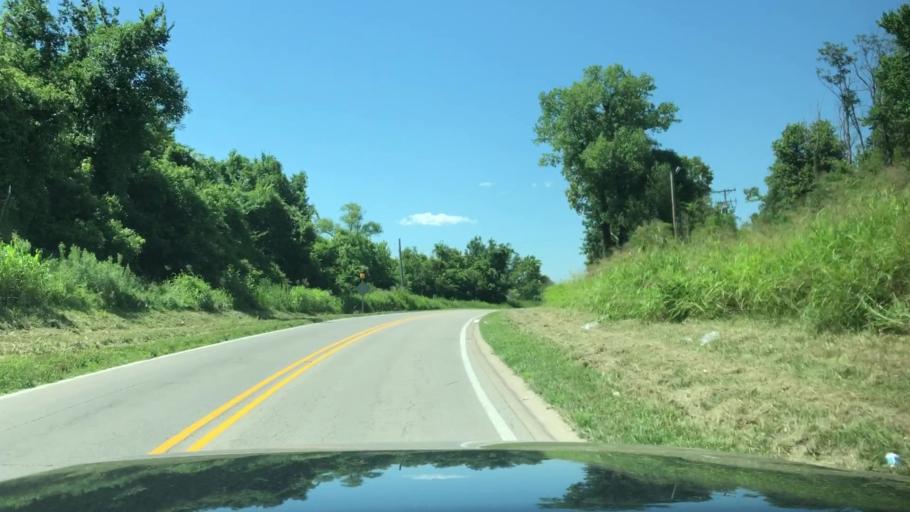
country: US
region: Illinois
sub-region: Saint Clair County
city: Centreville
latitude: 38.5554
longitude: -90.0976
